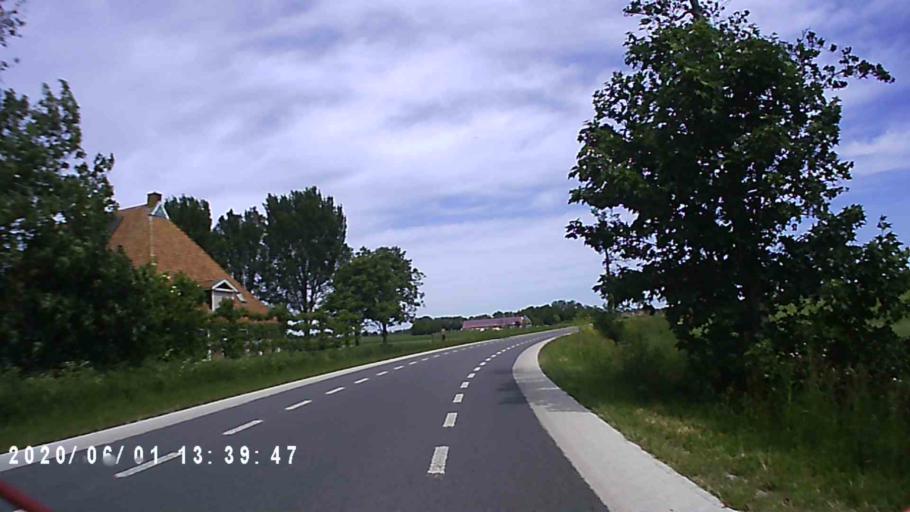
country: NL
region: Friesland
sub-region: Gemeente Littenseradiel
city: Wommels
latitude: 53.0877
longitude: 5.6012
